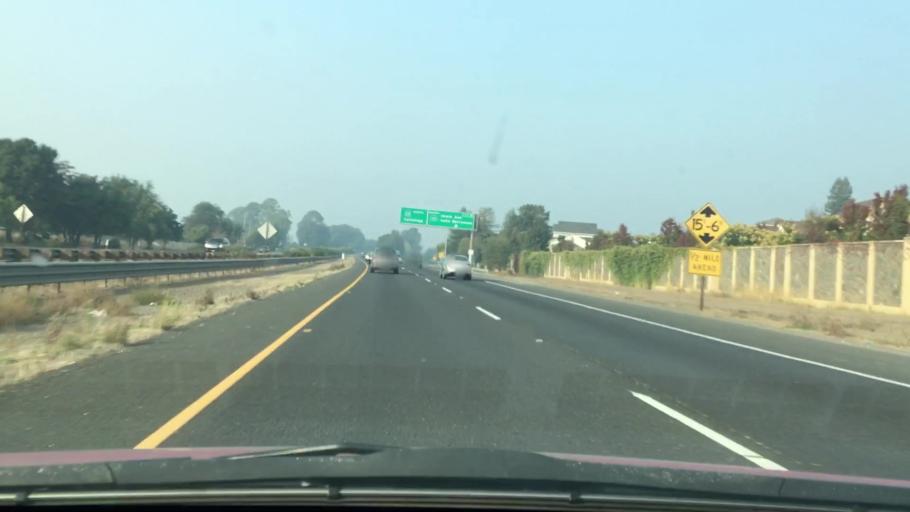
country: US
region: California
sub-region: Napa County
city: Napa
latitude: 38.2760
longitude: -122.2990
